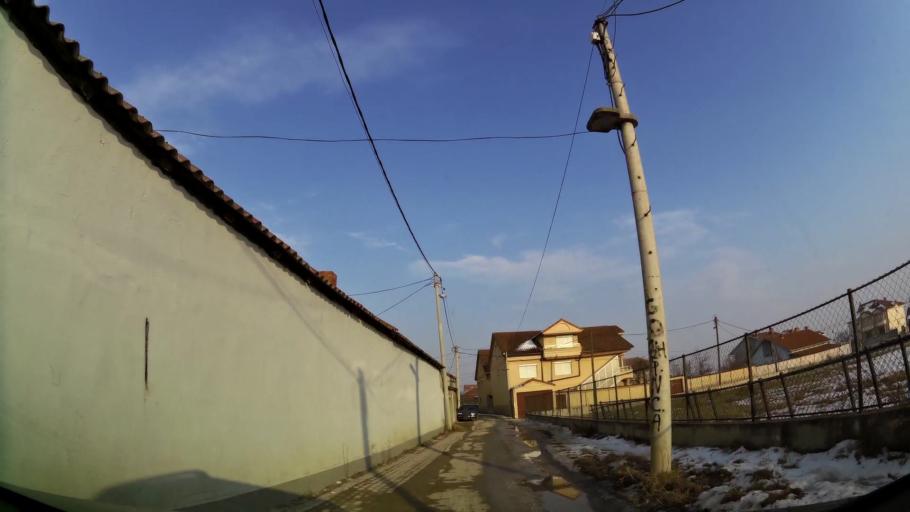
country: MK
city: Creshevo
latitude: 42.0226
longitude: 21.5212
